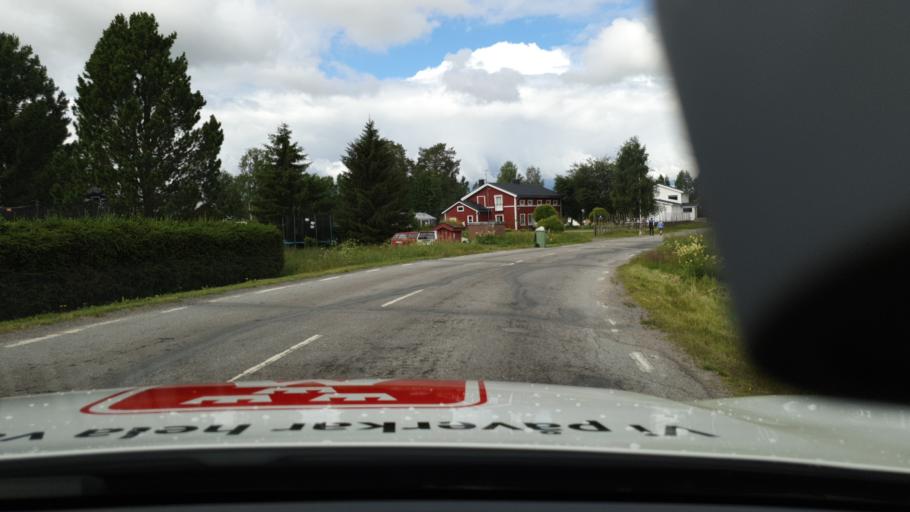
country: SE
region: Norrbotten
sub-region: Bodens Kommun
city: Saevast
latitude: 65.6059
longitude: 21.7030
